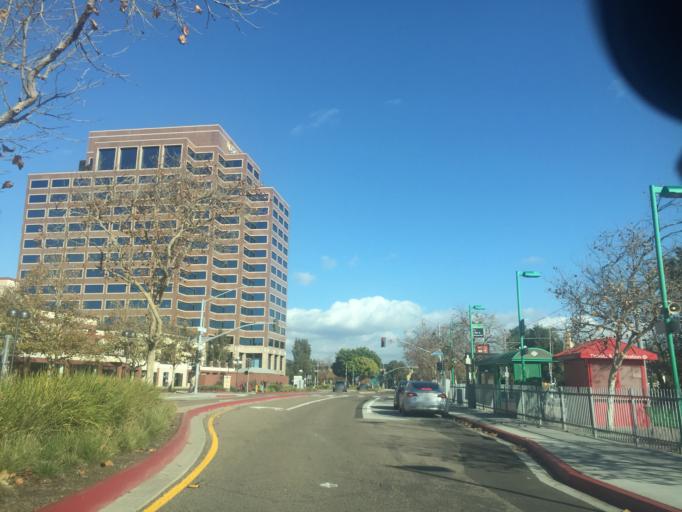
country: US
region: California
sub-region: San Diego County
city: San Diego
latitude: 32.7704
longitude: -117.1584
